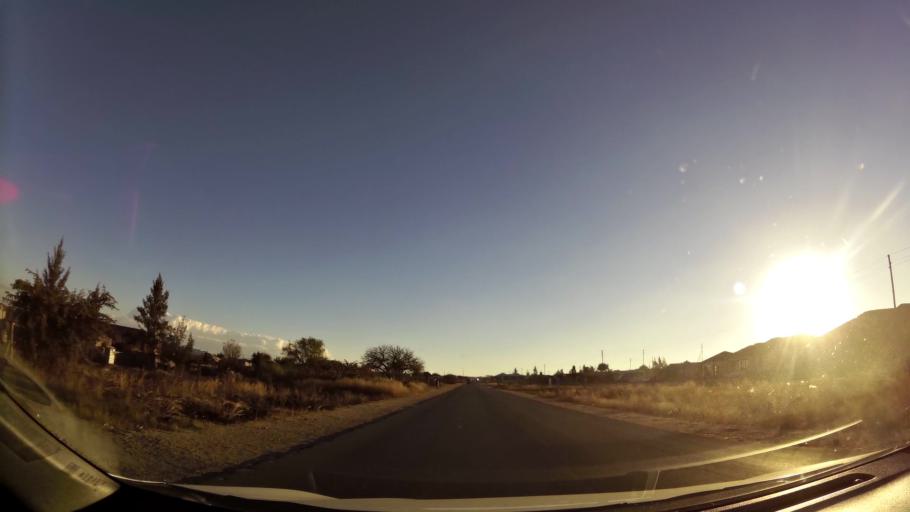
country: ZA
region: Limpopo
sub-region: Capricorn District Municipality
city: Polokwane
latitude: -23.8379
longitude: 29.3540
